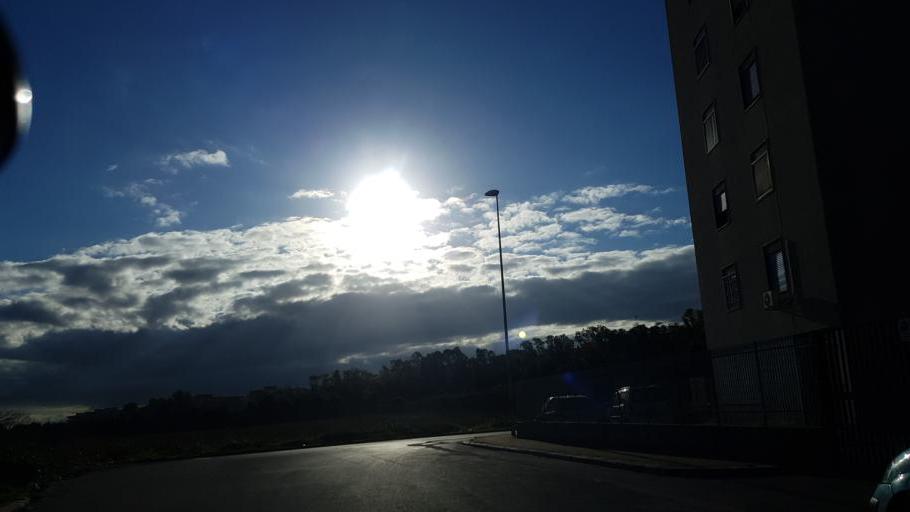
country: IT
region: Apulia
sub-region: Provincia di Brindisi
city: Brindisi
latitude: 40.6225
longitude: 17.9266
